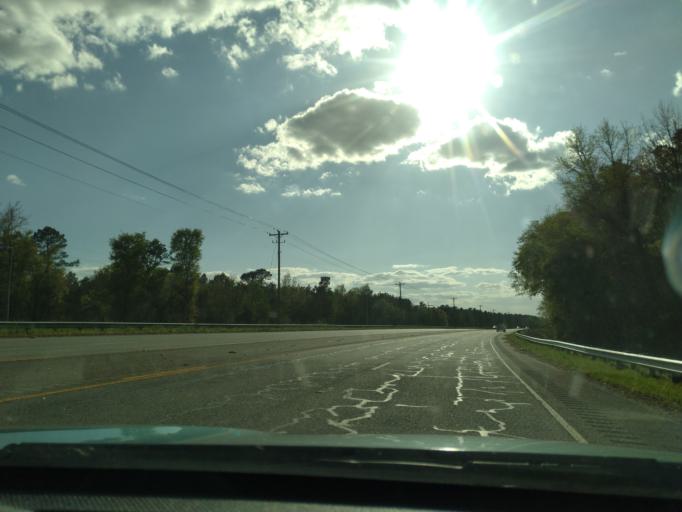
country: US
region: South Carolina
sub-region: Williamsburg County
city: Kingstree
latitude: 33.6580
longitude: -79.8544
